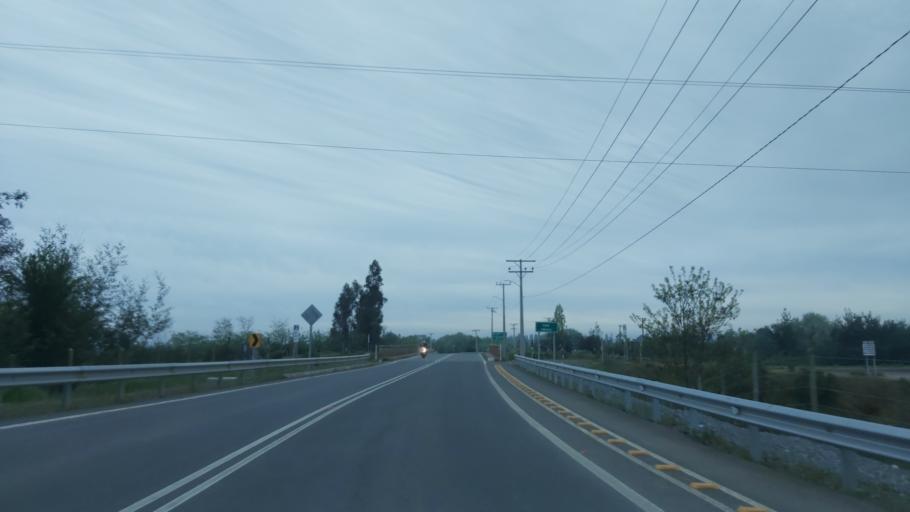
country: CL
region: Maule
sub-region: Provincia de Linares
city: Colbun
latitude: -35.6969
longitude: -71.4865
